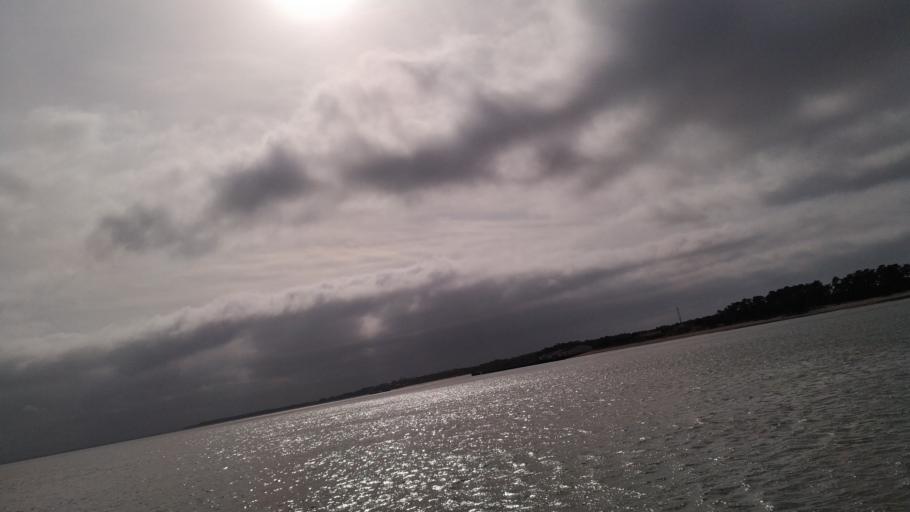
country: PT
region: Setubal
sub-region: Setubal
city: Setubal
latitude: 38.4838
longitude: -8.8739
